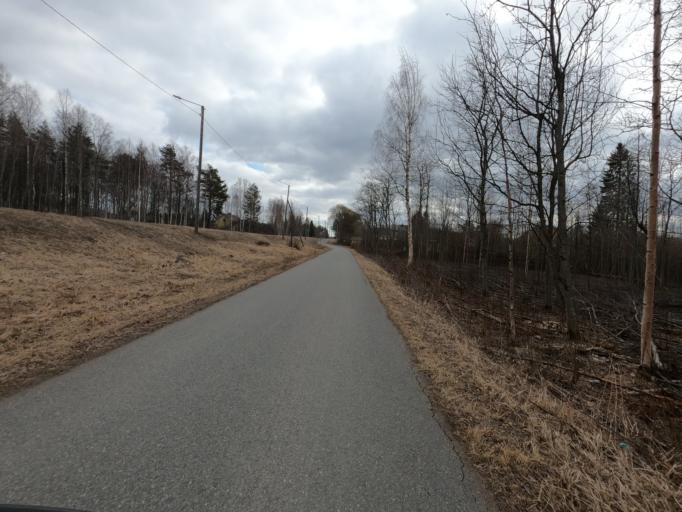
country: FI
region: North Karelia
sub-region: Joensuu
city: Joensuu
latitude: 62.5657
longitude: 29.8100
